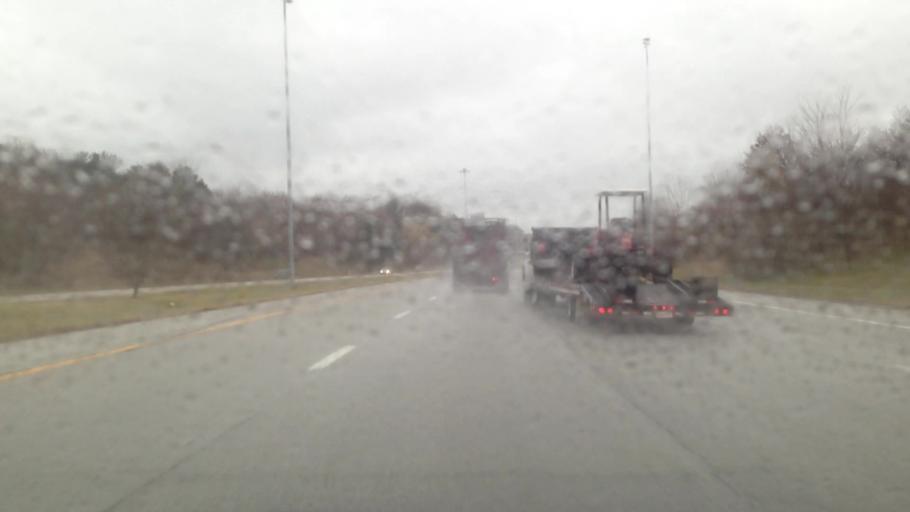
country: US
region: Ohio
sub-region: Lake County
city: Wickliffe
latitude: 41.5910
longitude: -81.4546
